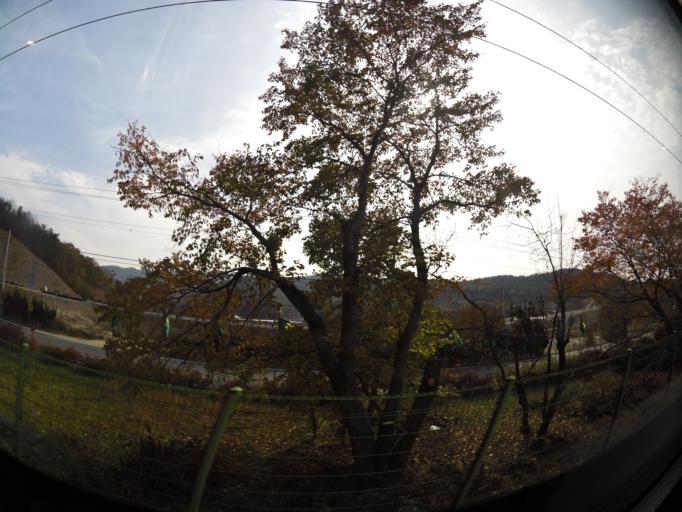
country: KR
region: Chungcheongbuk-do
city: Yong-dong
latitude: 36.1889
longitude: 127.8539
